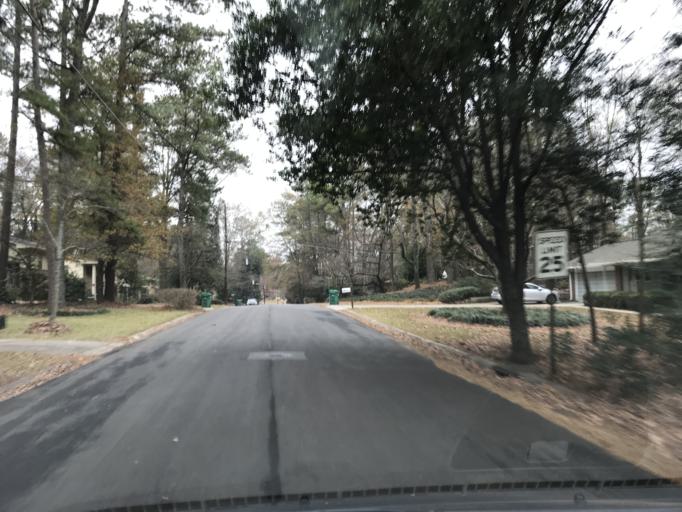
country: US
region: Georgia
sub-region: DeKalb County
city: Clarkston
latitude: 33.8226
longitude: -84.2536
